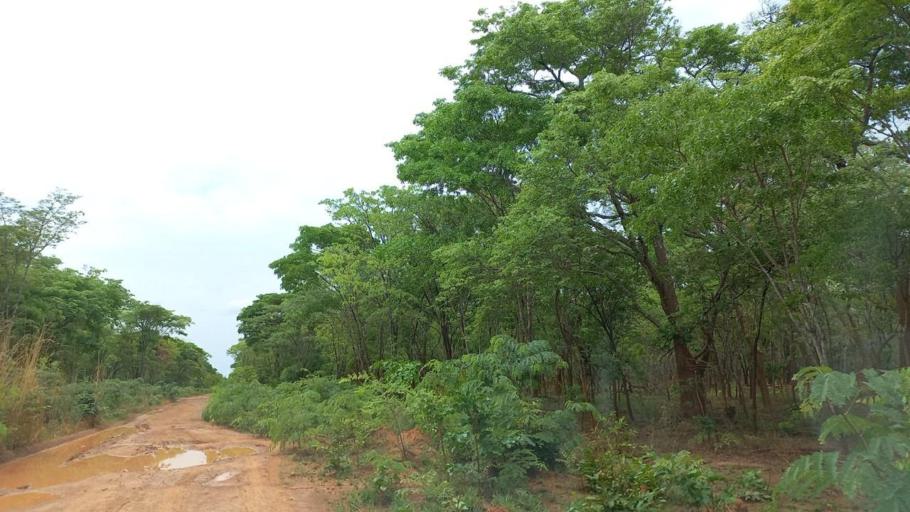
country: ZM
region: North-Western
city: Kalengwa
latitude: -13.5982
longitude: 24.9739
